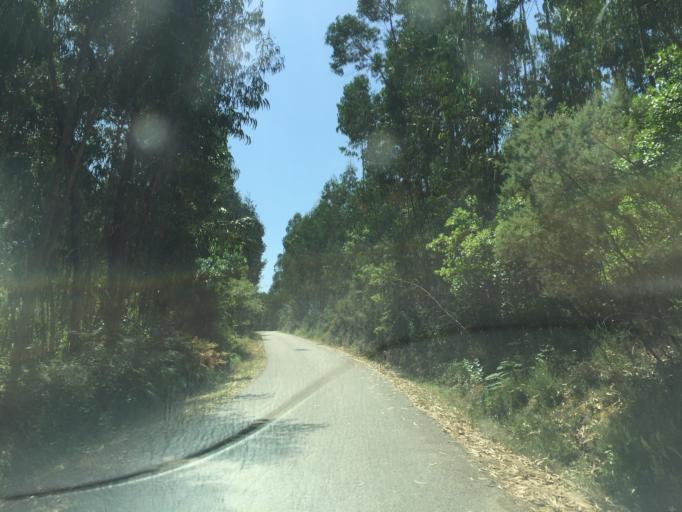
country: PT
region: Santarem
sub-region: Ferreira do Zezere
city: Ferreira do Zezere
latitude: 39.6480
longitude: -8.3002
